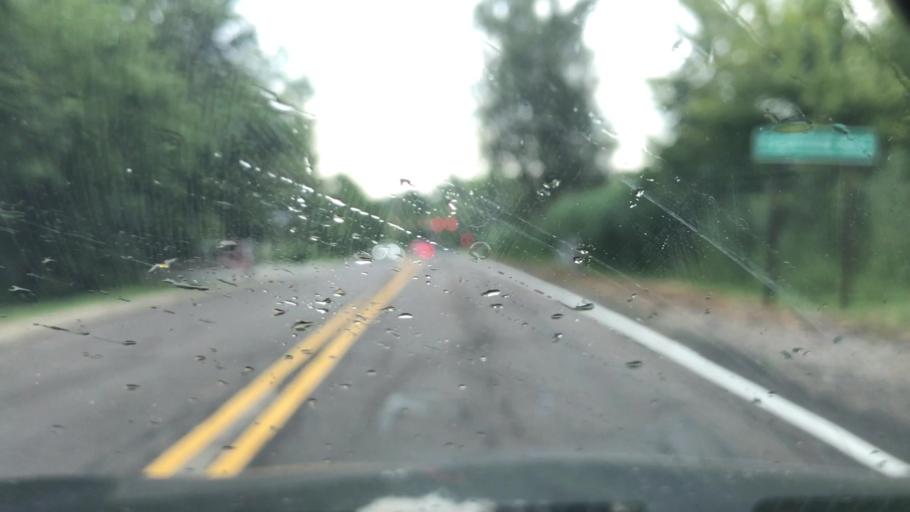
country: US
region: Michigan
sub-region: Oakland County
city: West Bloomfield Township
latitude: 42.5252
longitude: -83.4187
